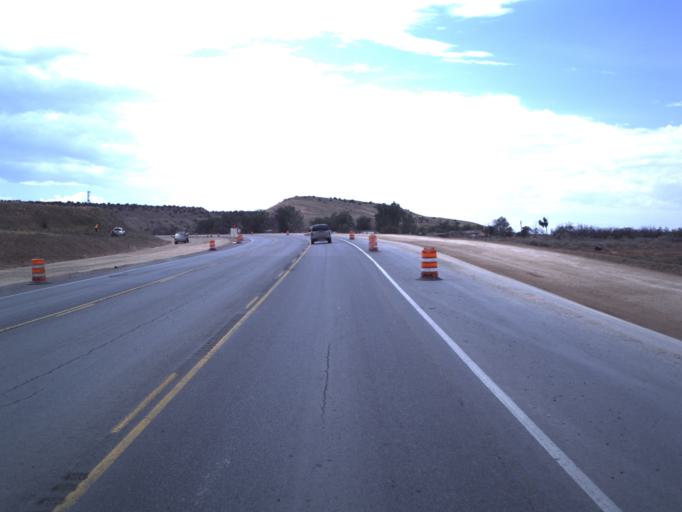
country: US
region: Utah
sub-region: Duchesne County
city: Roosevelt
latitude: 40.2576
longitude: -110.0621
